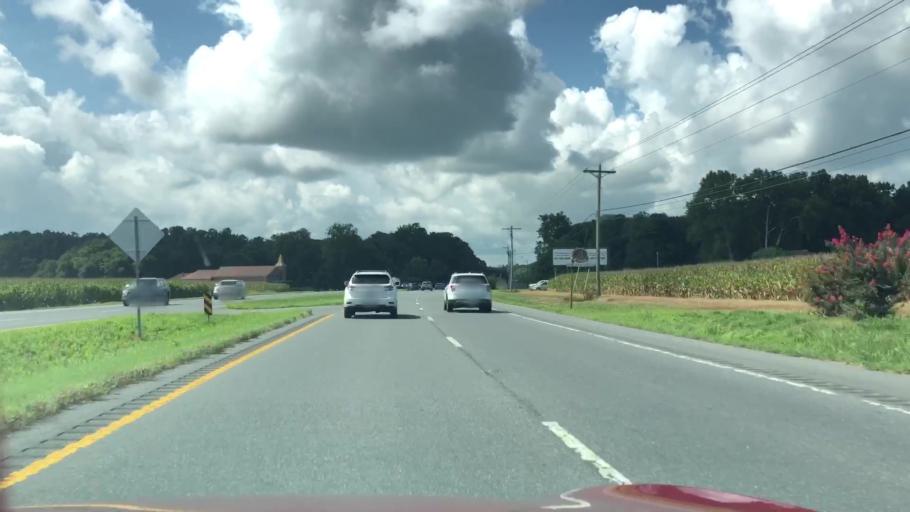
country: US
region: Virginia
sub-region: Accomack County
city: Accomac
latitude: 37.7606
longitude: -75.6168
